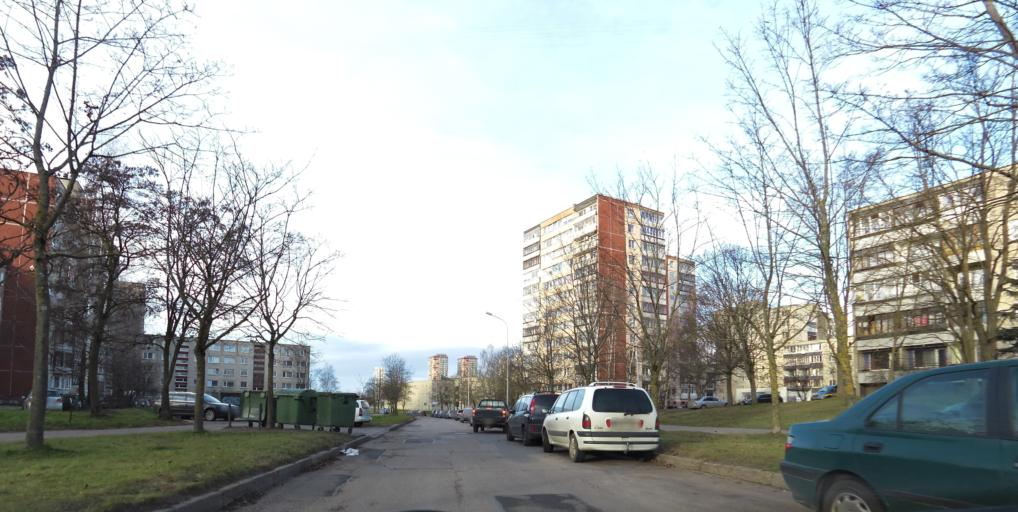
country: LT
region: Vilnius County
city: Justiniskes
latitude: 54.6971
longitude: 25.2254
